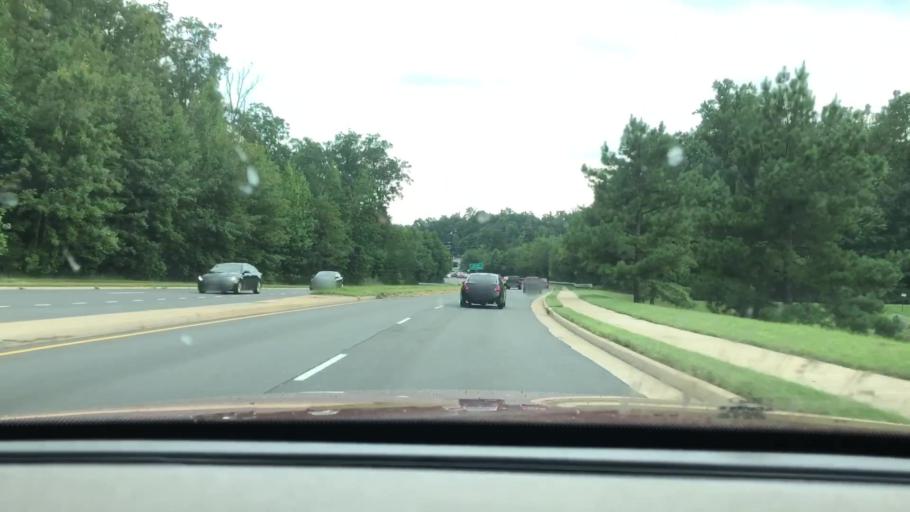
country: US
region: Virginia
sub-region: Fairfax County
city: Centreville
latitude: 38.8435
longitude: -77.4033
